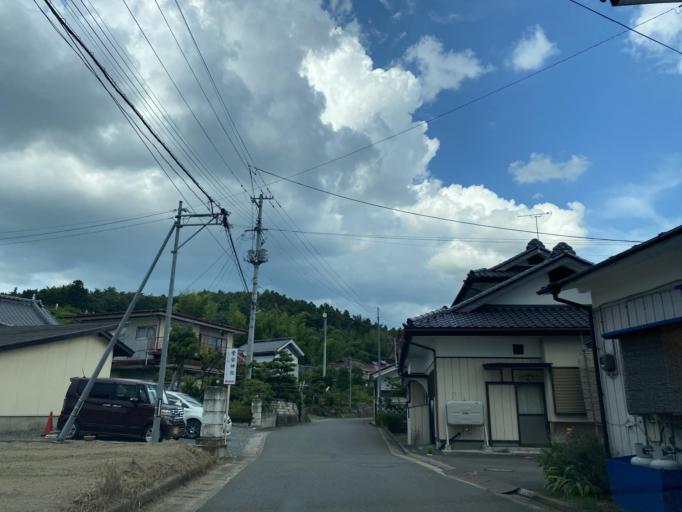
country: JP
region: Fukushima
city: Koriyama
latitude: 37.3711
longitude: 140.4301
